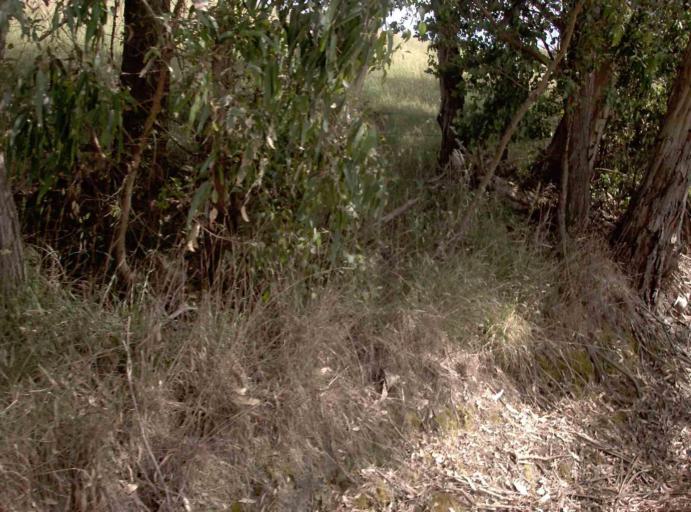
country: AU
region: Victoria
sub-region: East Gippsland
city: Lakes Entrance
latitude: -37.5193
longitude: 148.1417
